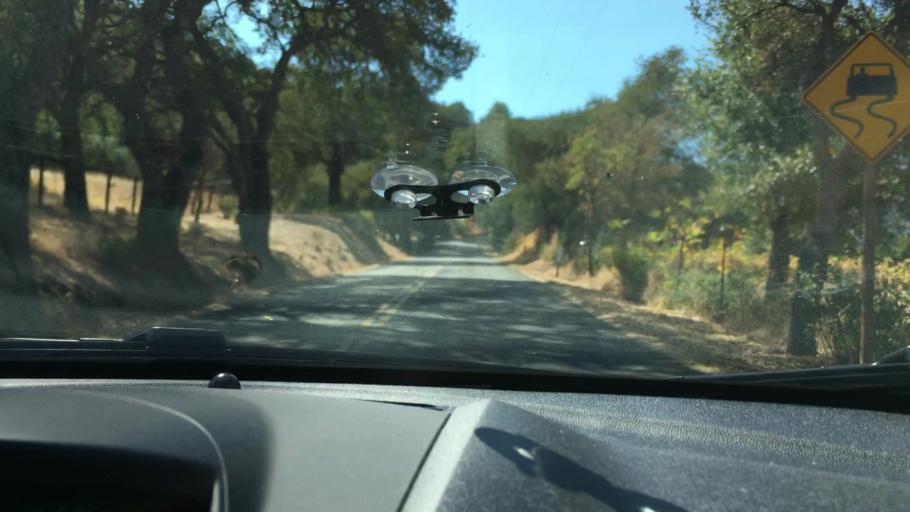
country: US
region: California
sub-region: Solano County
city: Green Valley
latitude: 38.3361
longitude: -122.1224
